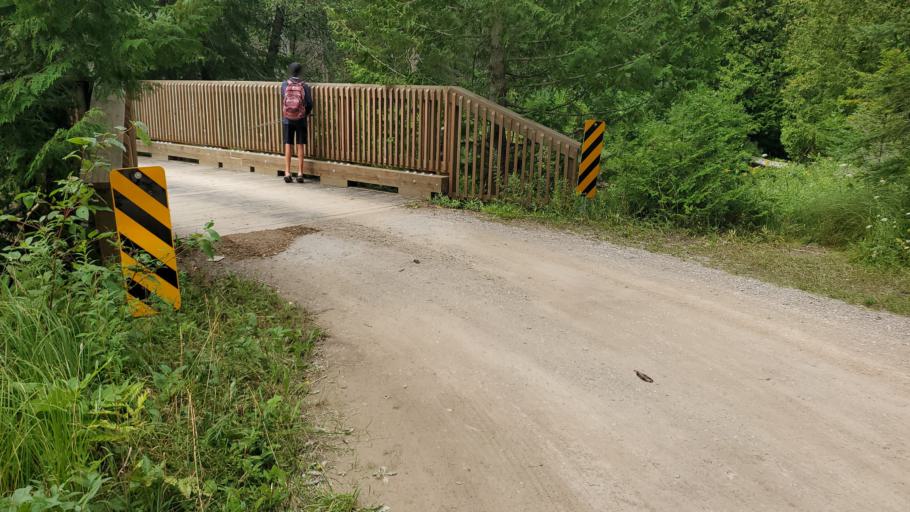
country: CA
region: Ontario
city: Tobermory
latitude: 45.1502
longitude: -81.4700
